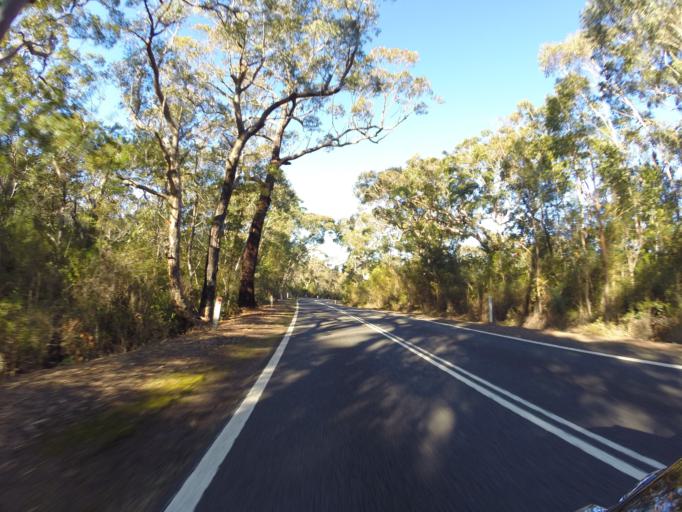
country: AU
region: New South Wales
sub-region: Wollongong
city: Helensburgh
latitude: -34.1460
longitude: 151.0071
